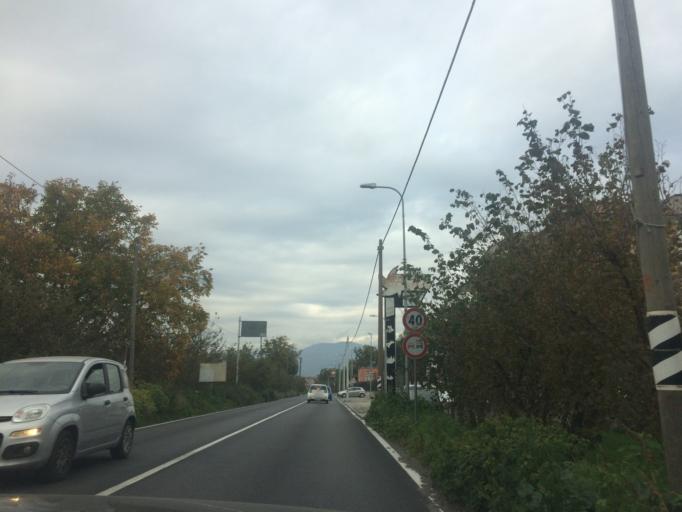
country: IT
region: Campania
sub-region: Provincia di Napoli
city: Piazzolla
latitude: 40.8983
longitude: 14.5242
